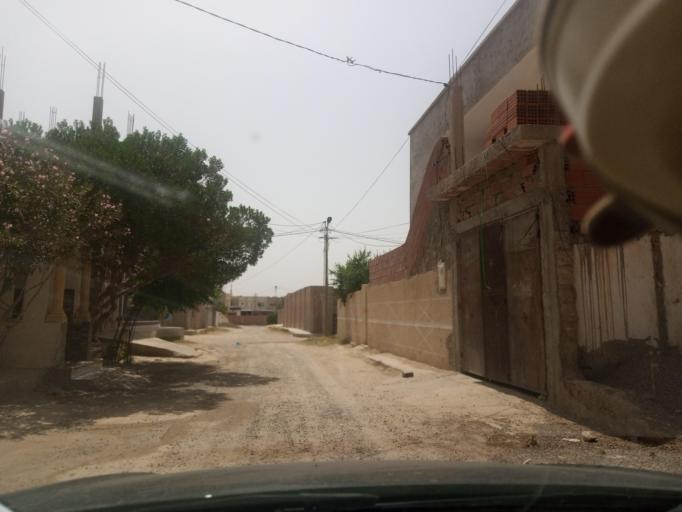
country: TN
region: Al Qasrayn
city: Kasserine
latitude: 35.2131
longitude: 8.8968
